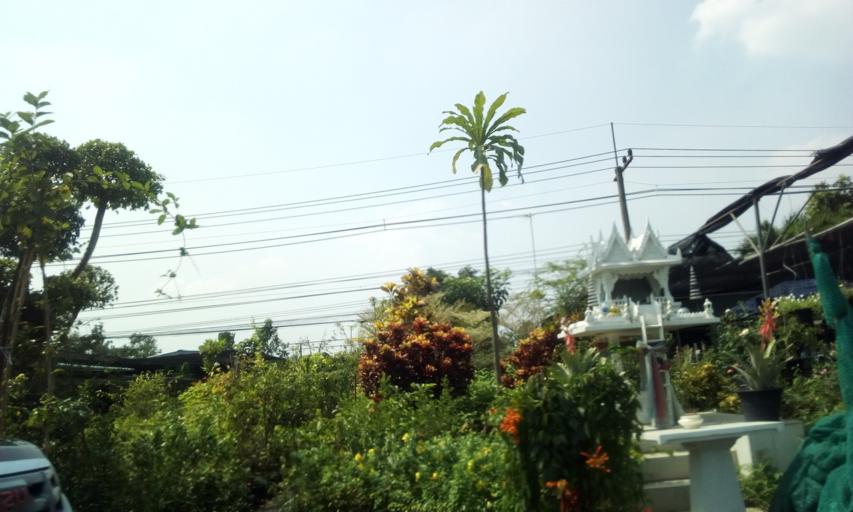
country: TH
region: Nakhon Nayok
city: Ongkharak
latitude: 14.1066
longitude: 100.9436
